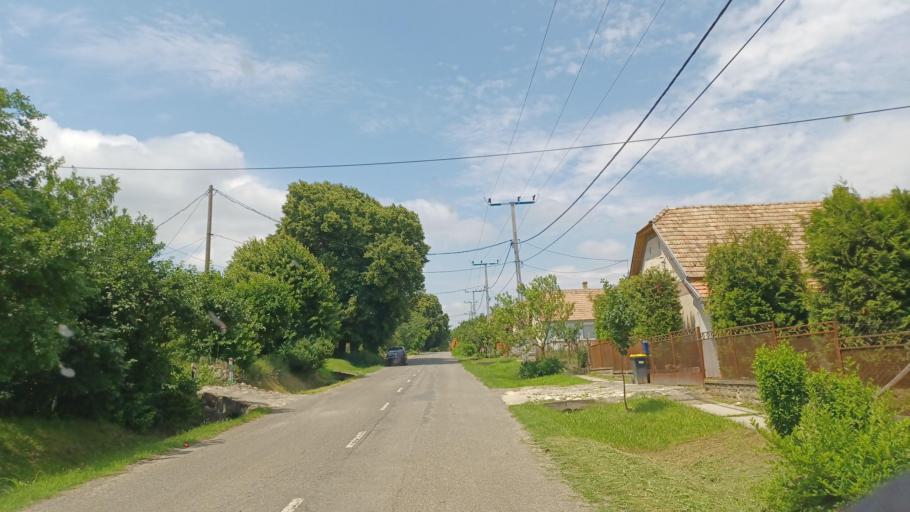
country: HU
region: Tolna
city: Simontornya
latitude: 46.6840
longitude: 18.5265
